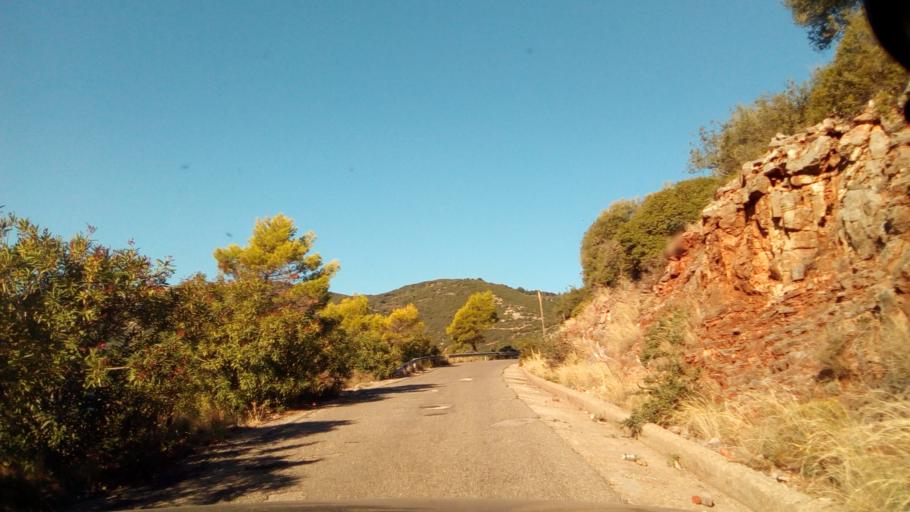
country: GR
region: West Greece
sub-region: Nomos Aitolias kai Akarnanias
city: Nafpaktos
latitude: 38.4153
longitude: 21.8450
